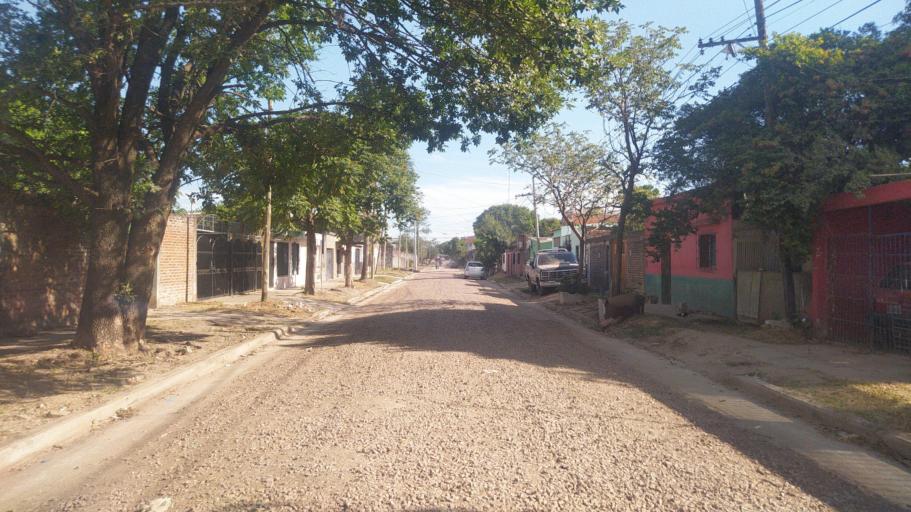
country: AR
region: Corrientes
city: Corrientes
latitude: -27.4905
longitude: -58.8155
